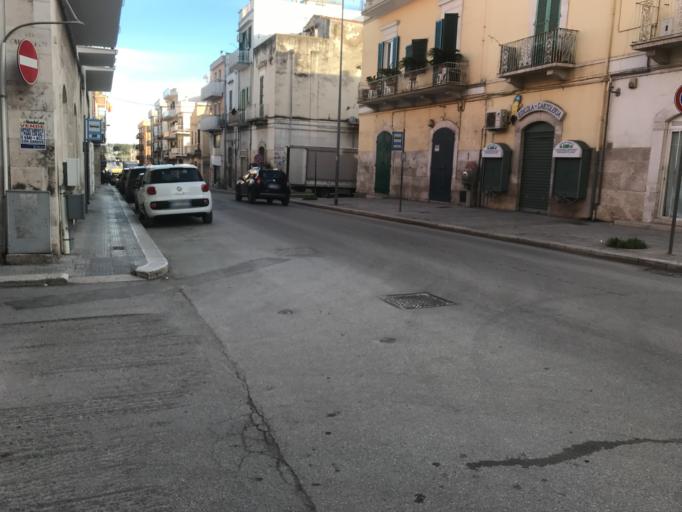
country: IT
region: Apulia
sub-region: Provincia di Bari
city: Corato
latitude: 41.1515
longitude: 16.4171
